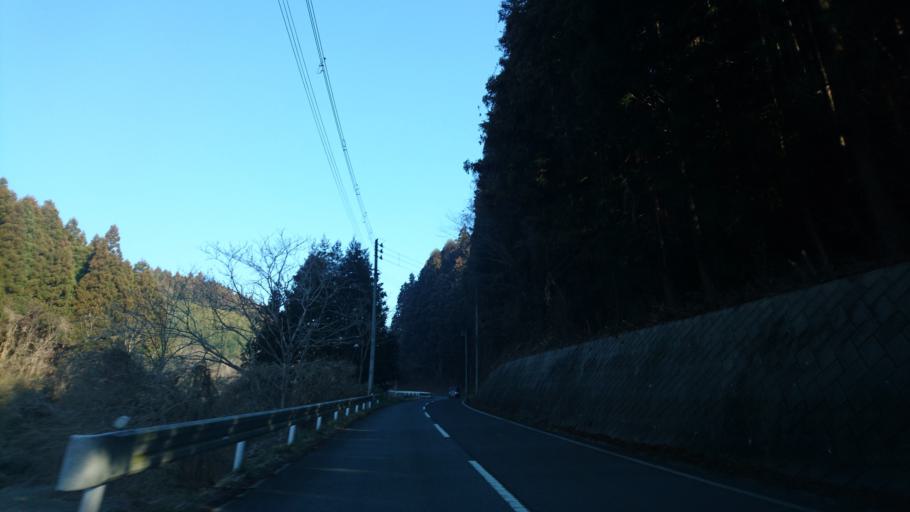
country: JP
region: Iwate
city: Ichinoseki
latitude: 38.9097
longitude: 141.2794
